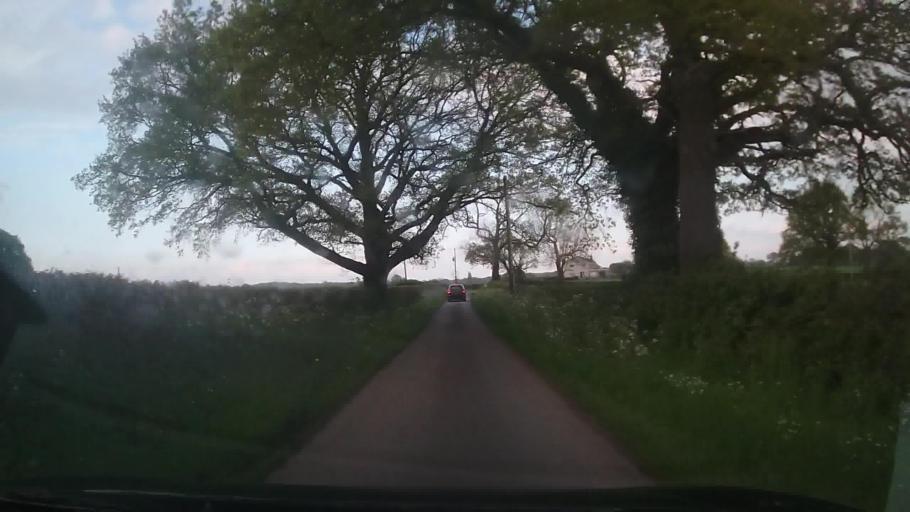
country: GB
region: England
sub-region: Shropshire
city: Ellesmere
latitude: 52.9321
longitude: -2.8489
